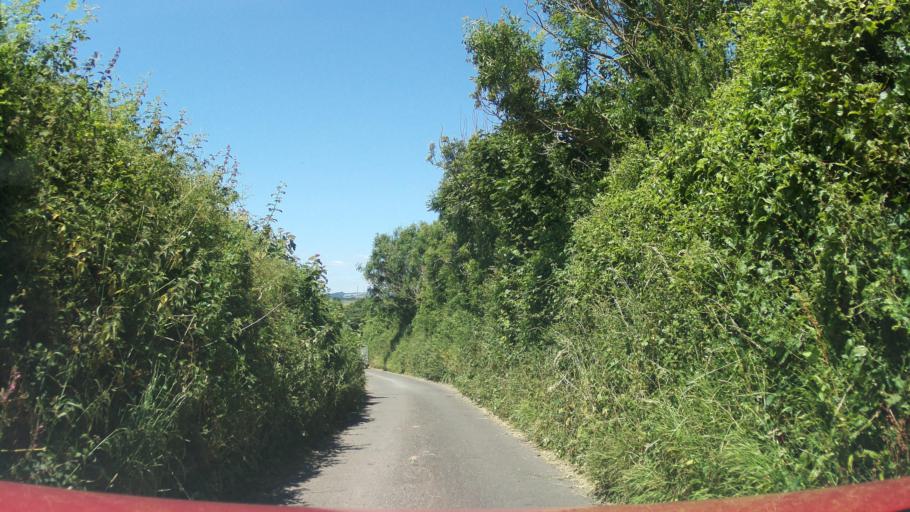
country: GB
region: England
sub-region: Devon
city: Dartmouth
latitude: 50.3911
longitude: -3.5635
